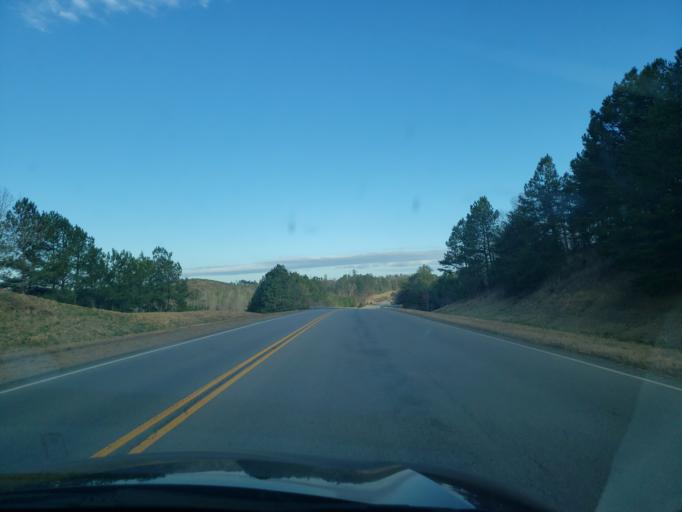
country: US
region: Alabama
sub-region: Cleburne County
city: Heflin
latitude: 33.4837
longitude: -85.5927
